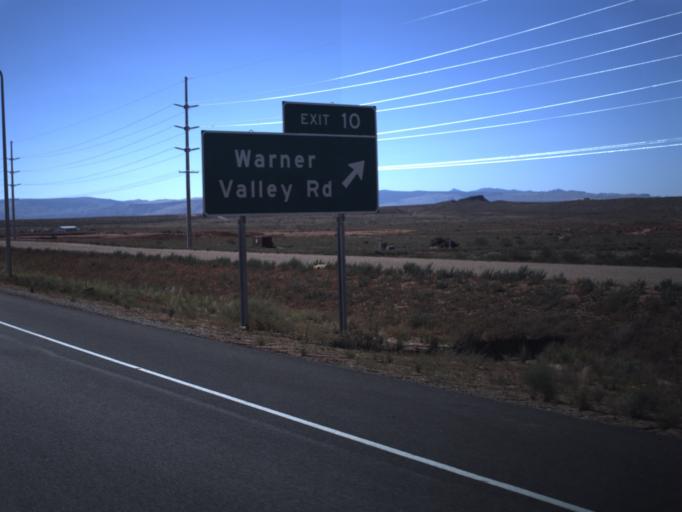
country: US
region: Utah
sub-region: Washington County
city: Washington
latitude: 37.0679
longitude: -113.4860
